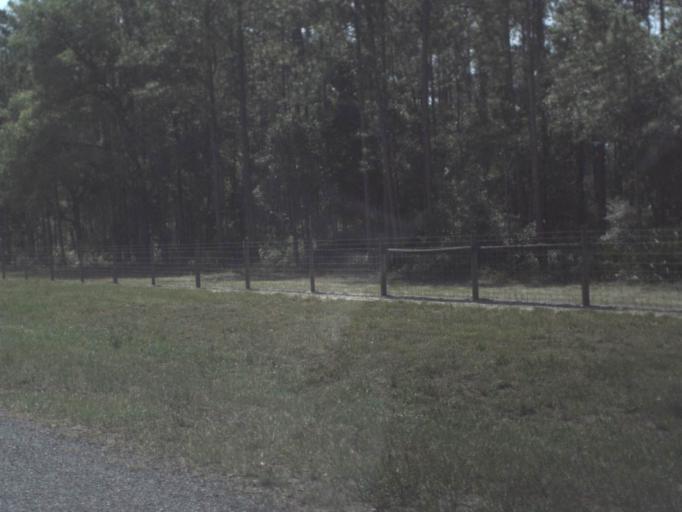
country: US
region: Florida
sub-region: Clay County
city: Middleburg
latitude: 29.9815
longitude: -81.9609
